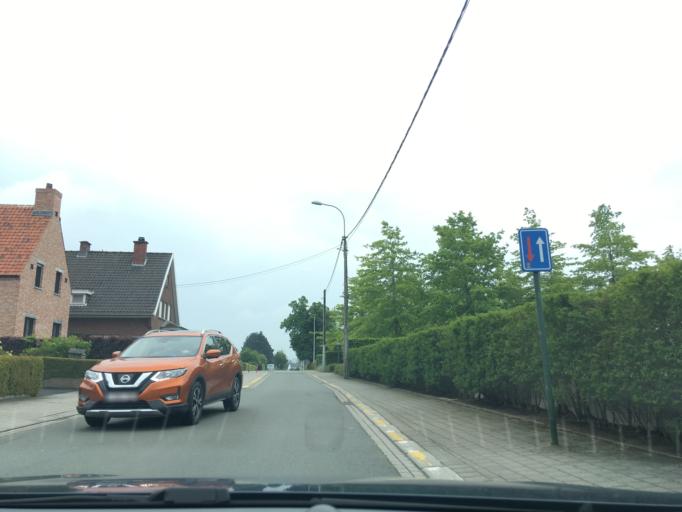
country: BE
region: Flanders
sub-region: Provincie West-Vlaanderen
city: Roeselare
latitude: 50.9302
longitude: 3.1597
